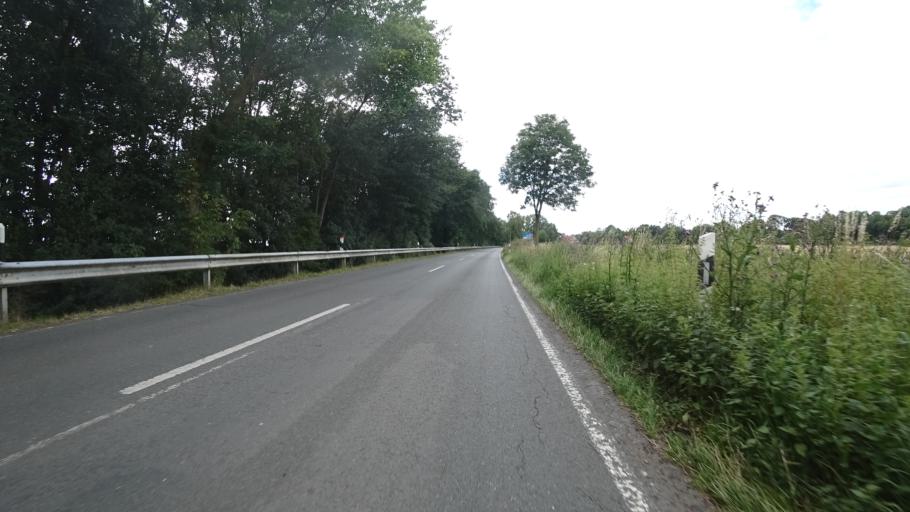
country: DE
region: Lower Saxony
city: Leese
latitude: 52.4765
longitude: 9.0881
